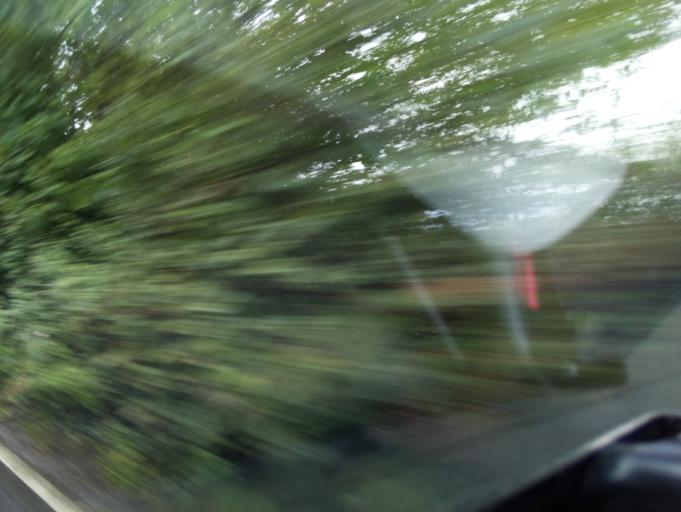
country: GB
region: England
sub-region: Devon
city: South Brent
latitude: 50.4144
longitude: -3.8354
